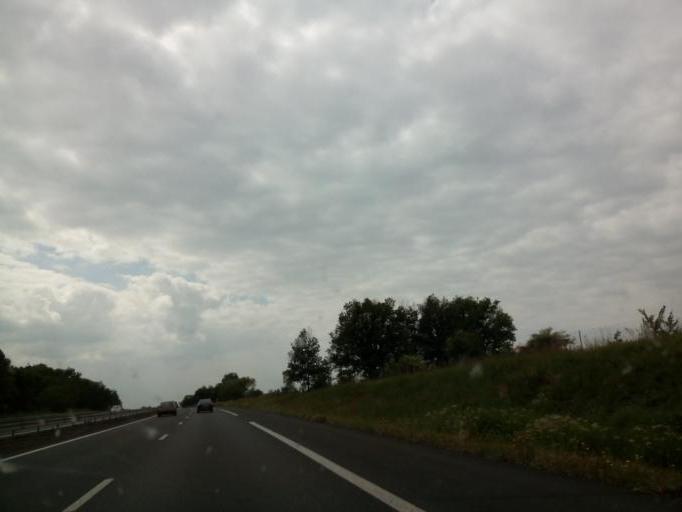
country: FR
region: Pays de la Loire
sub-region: Departement de Maine-et-Loire
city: Ingrandes
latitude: 47.4283
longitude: -0.9173
